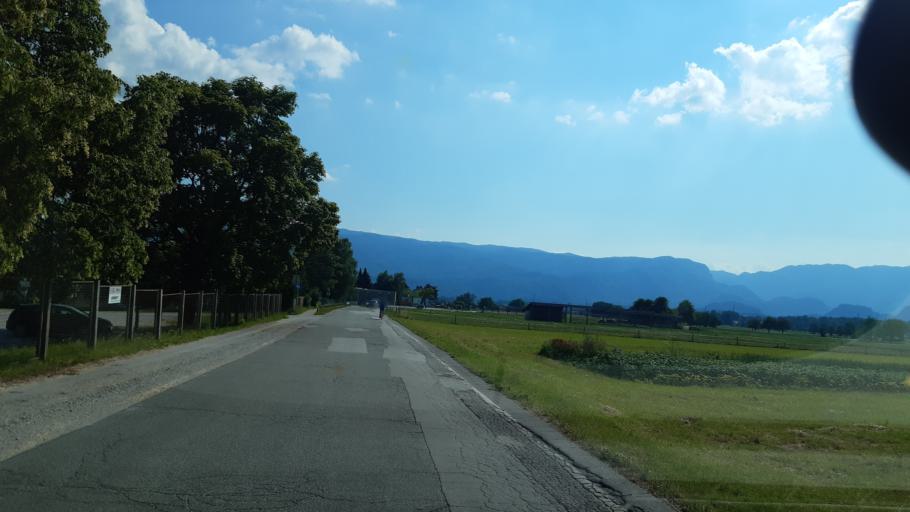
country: SI
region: Radovljica
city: Radovljica
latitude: 46.3736
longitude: 14.1973
